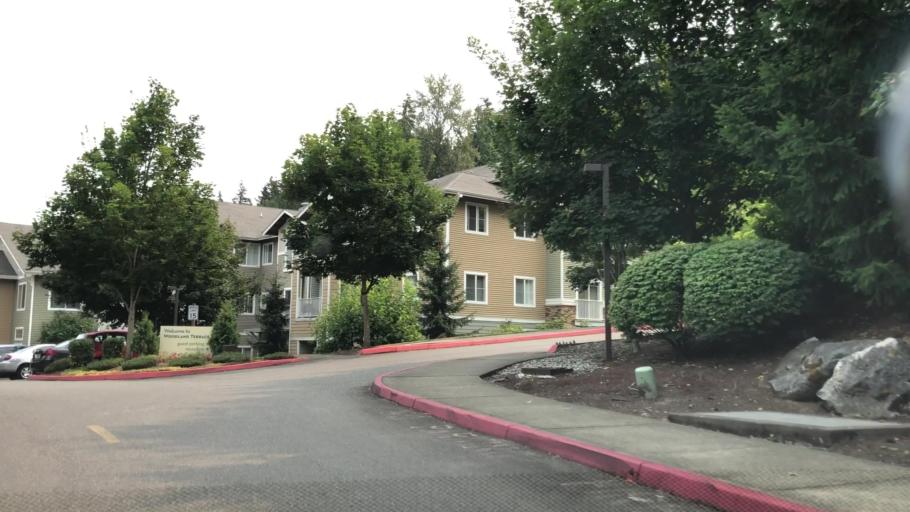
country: US
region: Washington
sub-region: King County
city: Bothell
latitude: 47.7548
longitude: -122.2031
